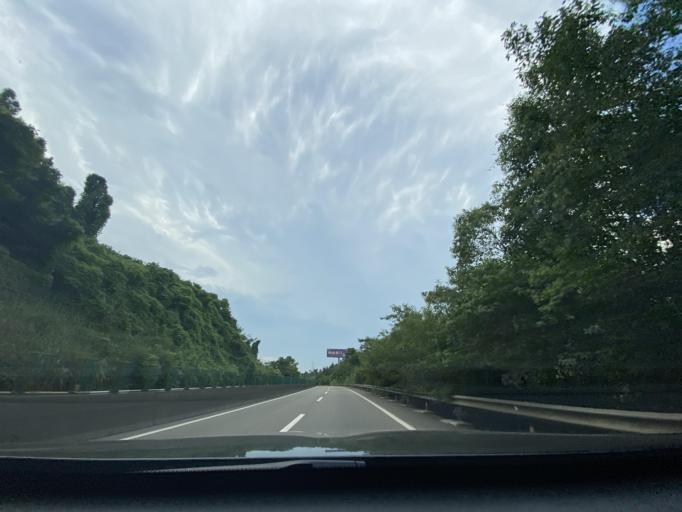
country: CN
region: Sichuan
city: Neijiang
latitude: 29.6577
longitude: 104.9829
